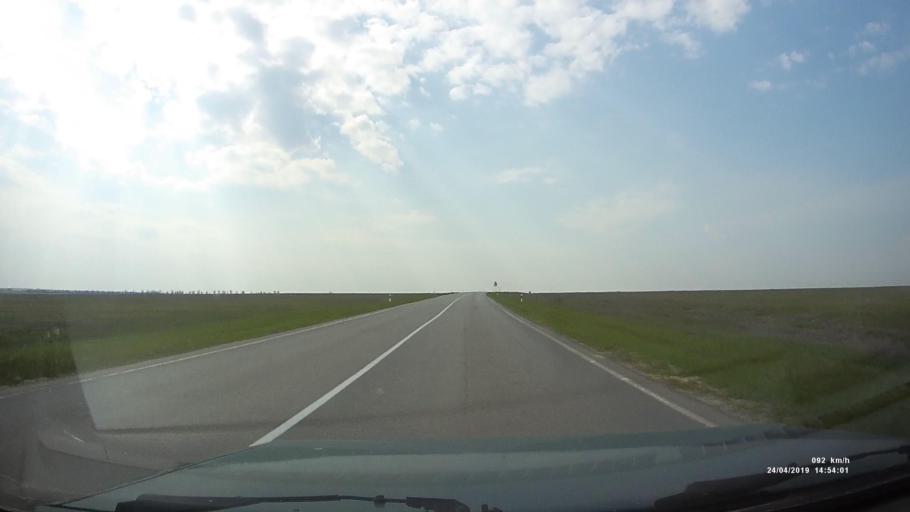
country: RU
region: Rostov
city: Remontnoye
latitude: 46.5322
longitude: 43.6467
